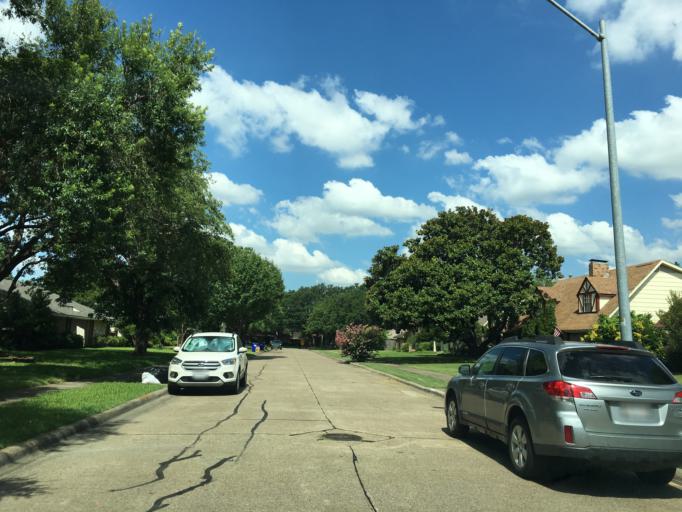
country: US
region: Texas
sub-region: Dallas County
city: Farmers Branch
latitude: 32.9258
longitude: -96.8761
